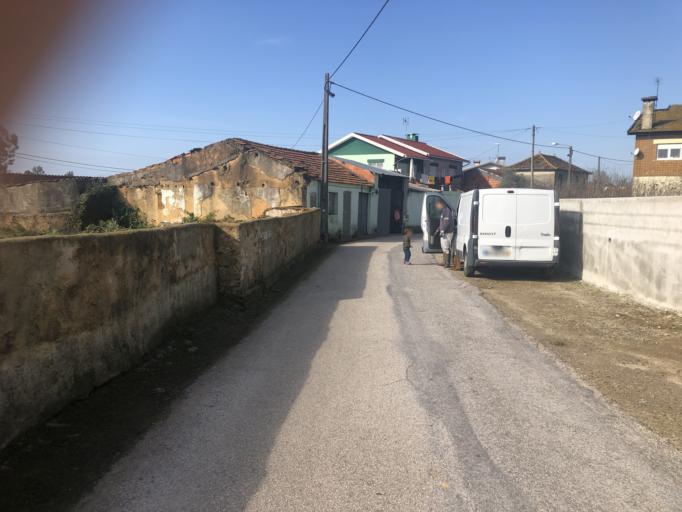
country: PT
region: Aveiro
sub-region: Estarreja
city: Beduido
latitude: 40.7672
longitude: -8.5471
